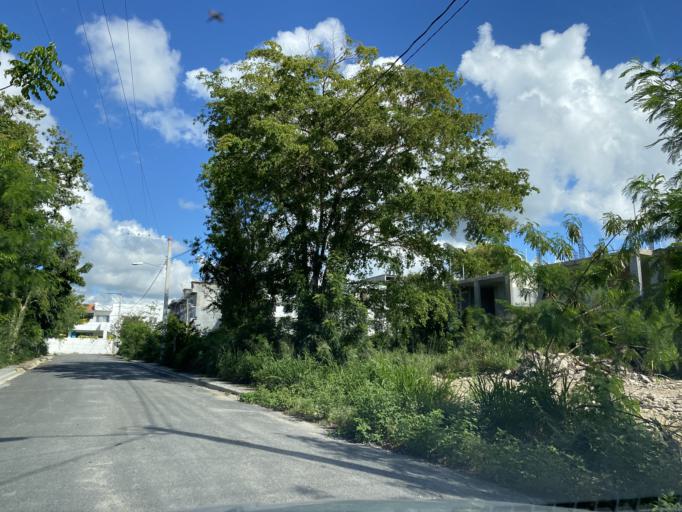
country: DO
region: La Romana
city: La Romana
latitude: 18.3686
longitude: -68.8358
